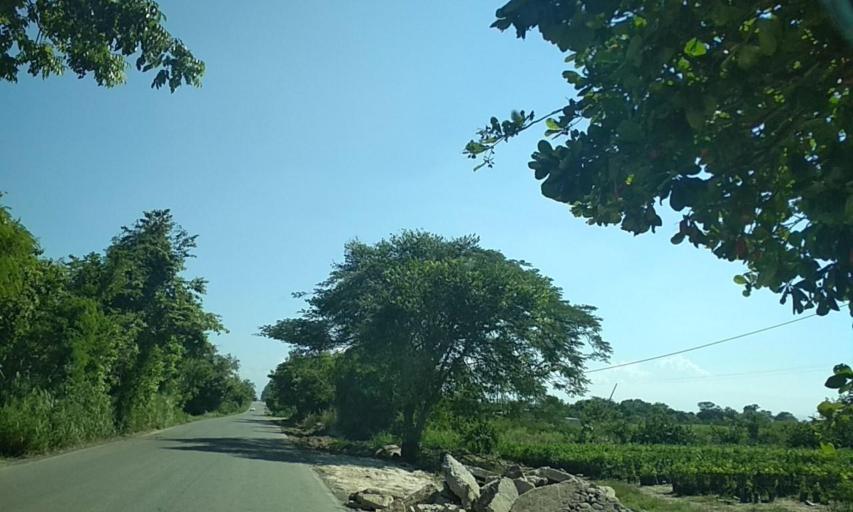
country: MX
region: Veracruz
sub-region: Martinez de la Torre
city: La Union Paso Largo
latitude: 20.1480
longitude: -97.0003
